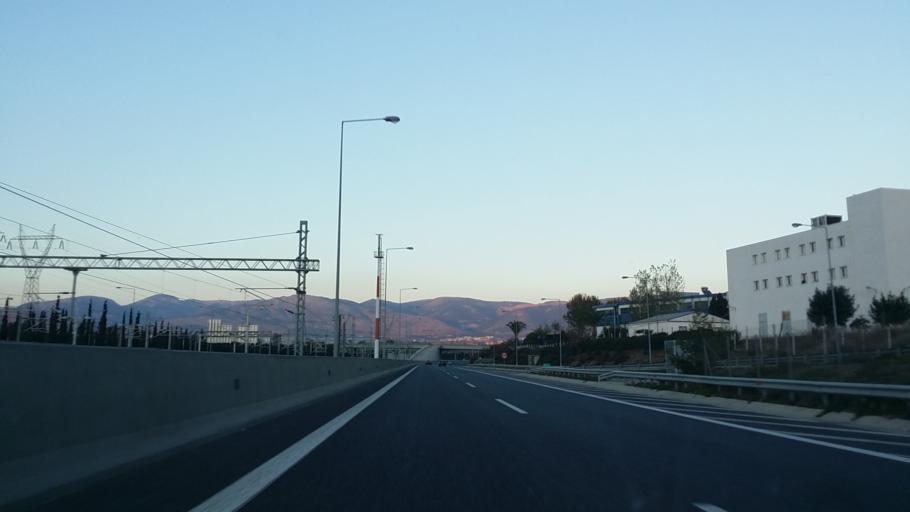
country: GR
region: Attica
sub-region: Nomarchia Dytikis Attikis
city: Magoula
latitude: 38.0740
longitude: 23.5302
